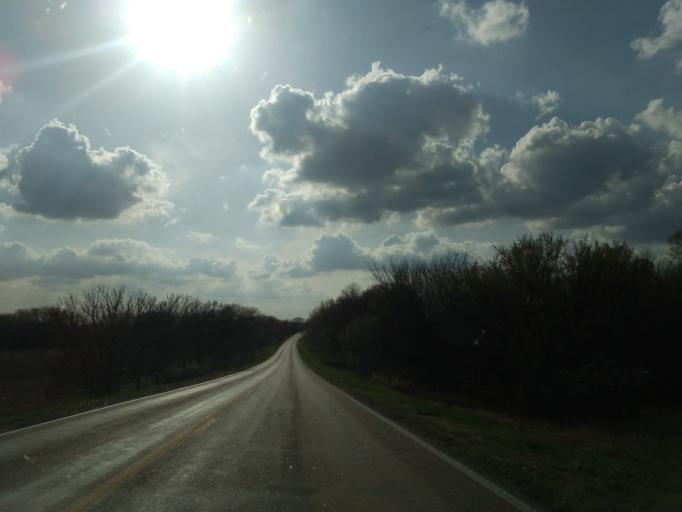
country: US
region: Nebraska
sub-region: Webster County
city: Red Cloud
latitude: 40.0890
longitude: -98.6028
